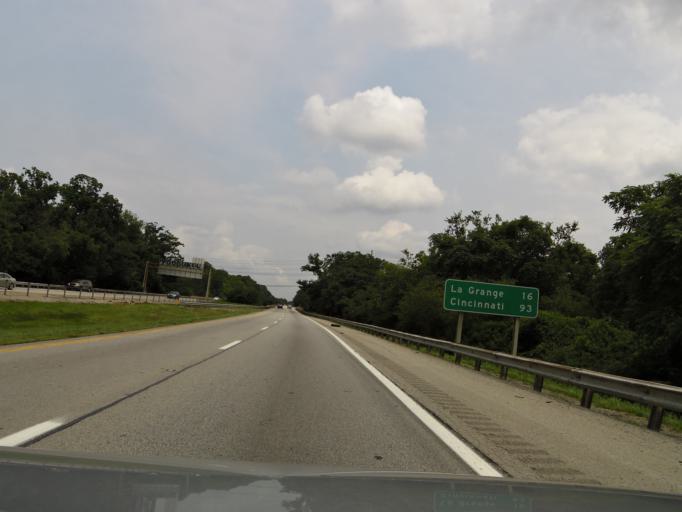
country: US
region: Kentucky
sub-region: Jefferson County
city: Northfield
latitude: 38.2945
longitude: -85.6296
